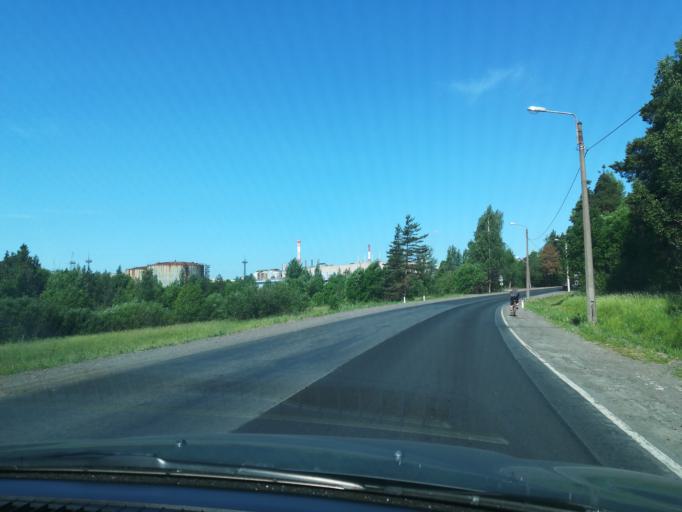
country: RU
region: Leningrad
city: Svetogorsk
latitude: 61.0984
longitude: 28.8758
